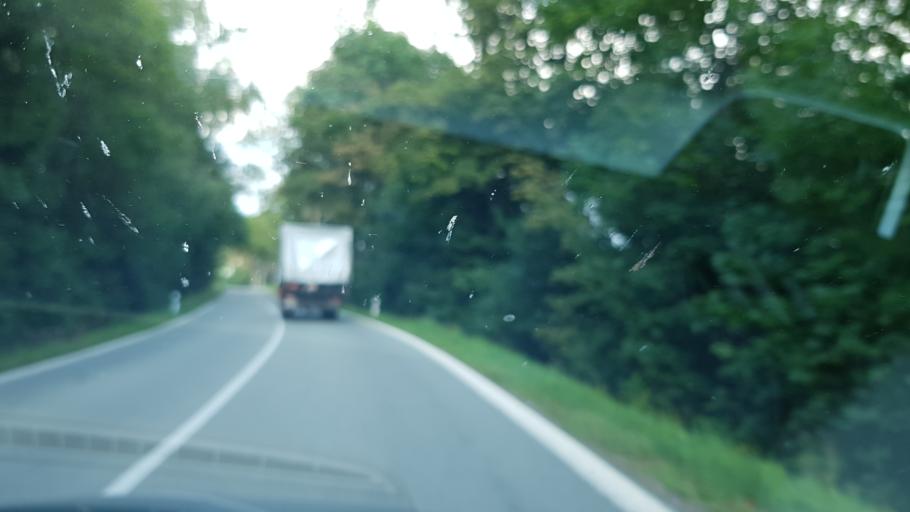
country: CZ
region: Pardubicky
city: Jablonne nad Orlici
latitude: 50.0923
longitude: 16.6092
